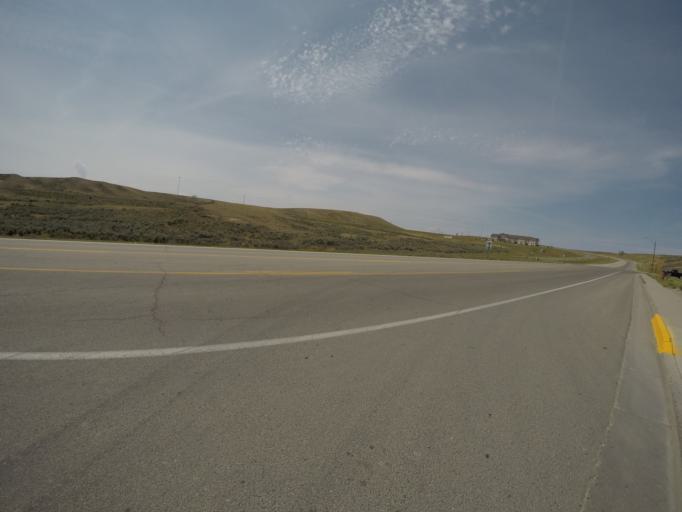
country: US
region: Wyoming
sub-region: Lincoln County
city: Kemmerer
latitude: 41.7732
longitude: -110.5450
